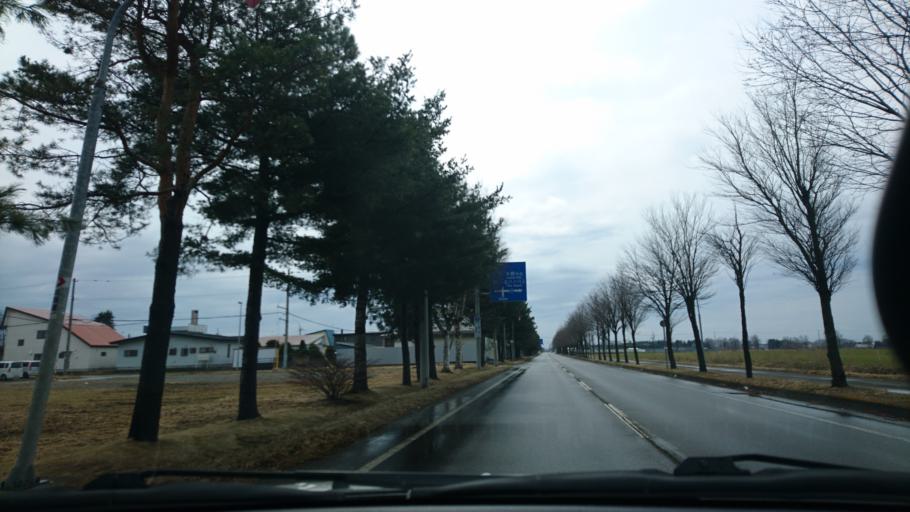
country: JP
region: Hokkaido
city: Otofuke
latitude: 42.9746
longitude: 143.1915
